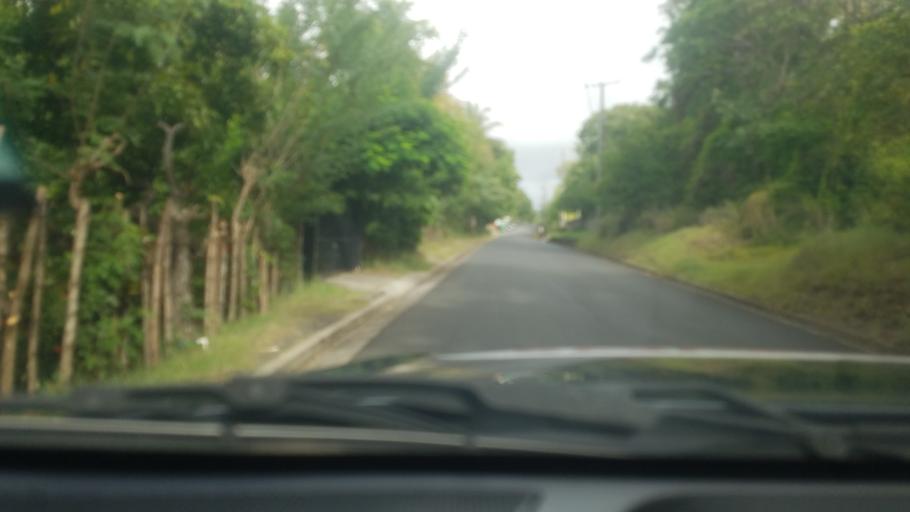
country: LC
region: Micoud Quarter
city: Micoud
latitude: 13.7955
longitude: -60.9099
